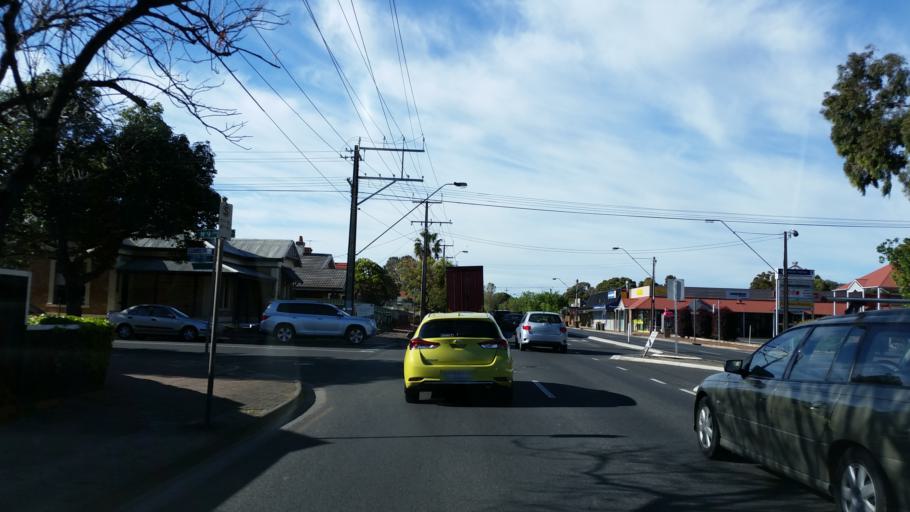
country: AU
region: South Australia
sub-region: Norwood Payneham St Peters
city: Royston Park
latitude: -34.9047
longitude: 138.6399
